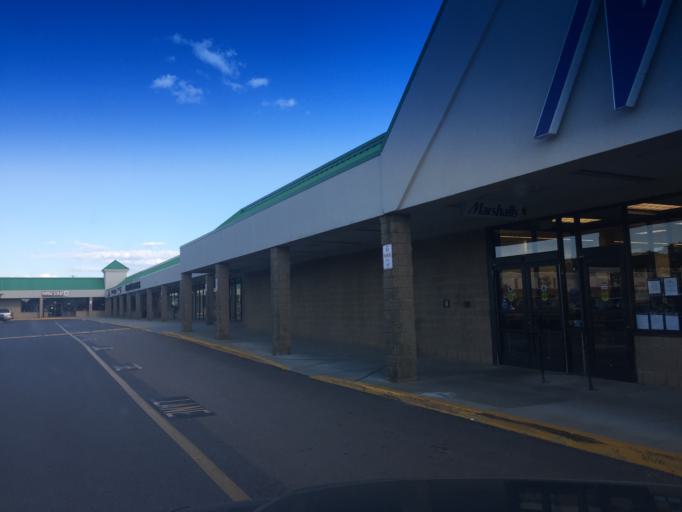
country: US
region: Massachusetts
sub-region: Norfolk County
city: Franklin
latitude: 42.0882
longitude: -71.4232
